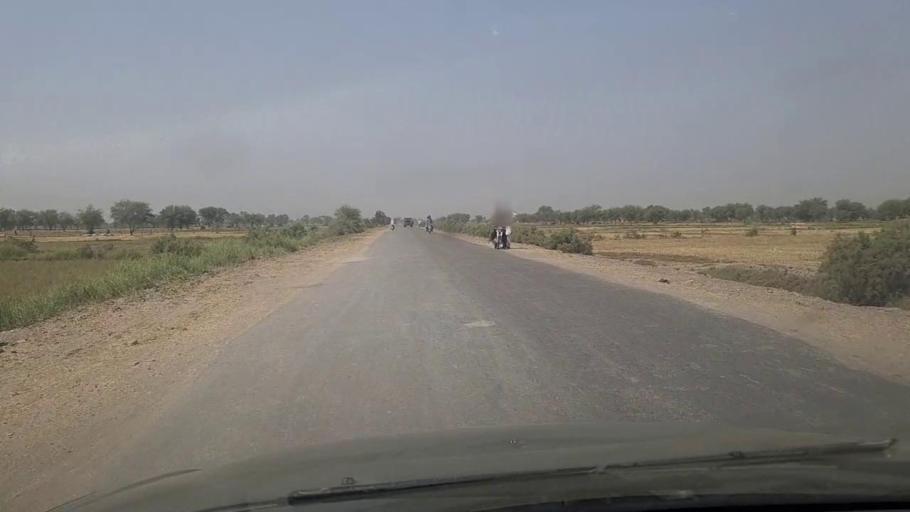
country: PK
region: Sindh
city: Khanpur
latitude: 27.9068
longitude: 69.5068
